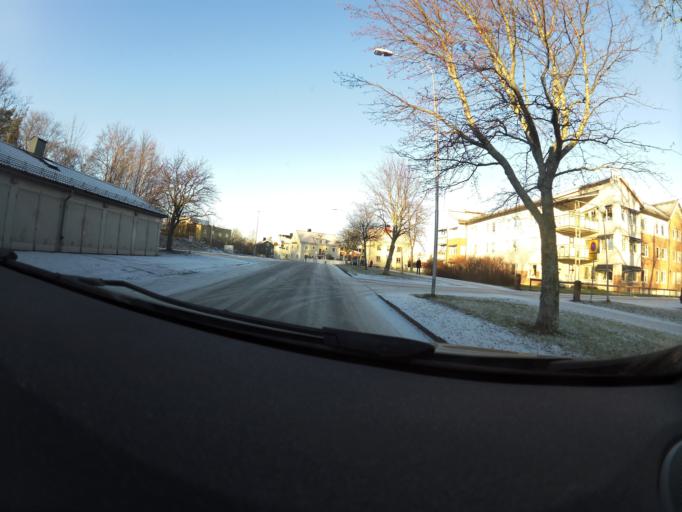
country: SE
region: Gaevleborg
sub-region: Gavle Kommun
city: Gavle
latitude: 60.6652
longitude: 17.1460
